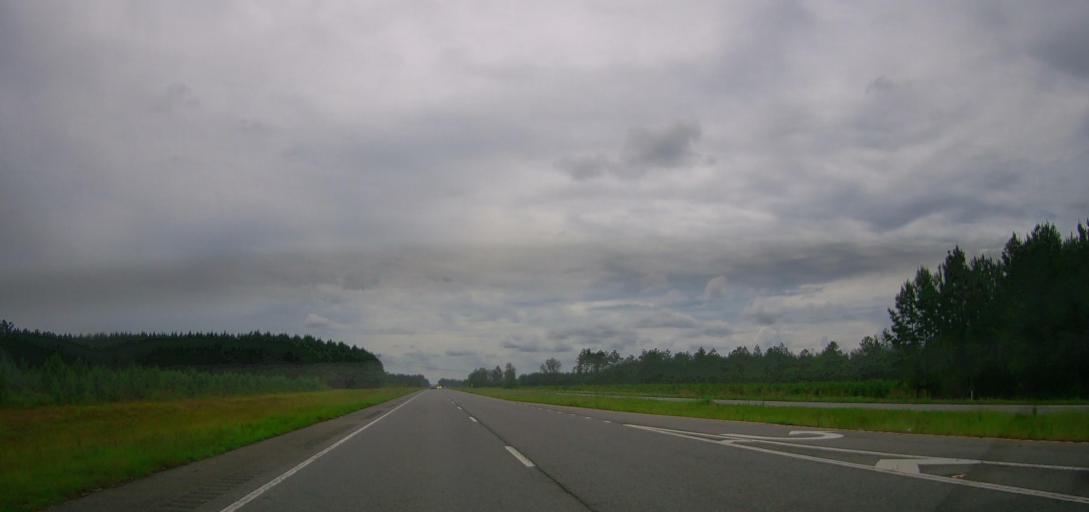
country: US
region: Georgia
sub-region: Appling County
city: Baxley
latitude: 31.7533
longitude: -82.2760
